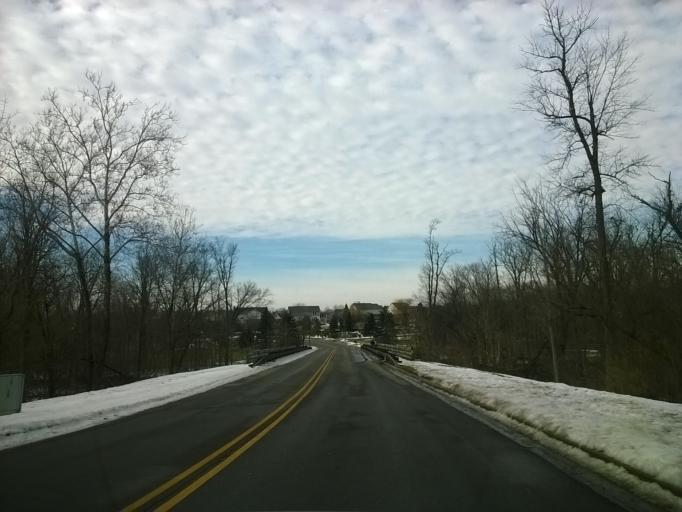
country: US
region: Indiana
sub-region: Boone County
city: Zionsville
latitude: 39.9773
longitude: -86.2484
